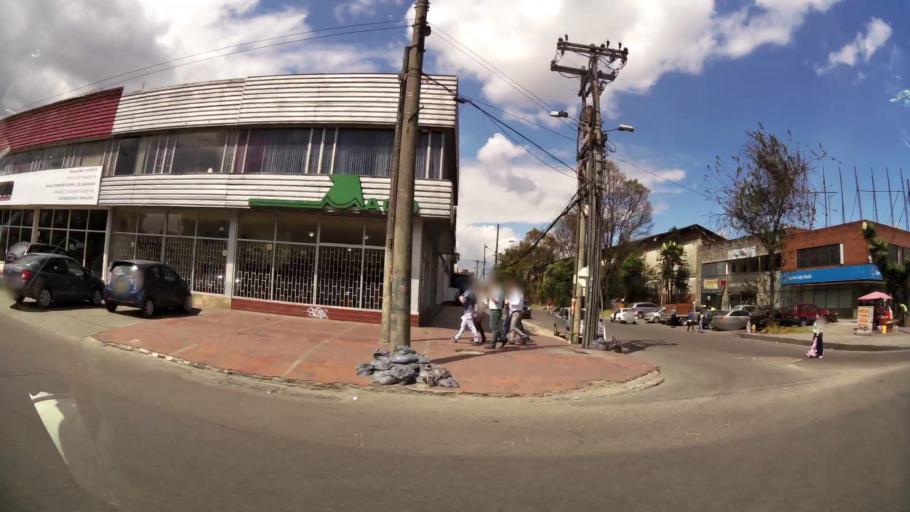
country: CO
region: Bogota D.C.
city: Bogota
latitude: 4.6335
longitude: -74.1132
